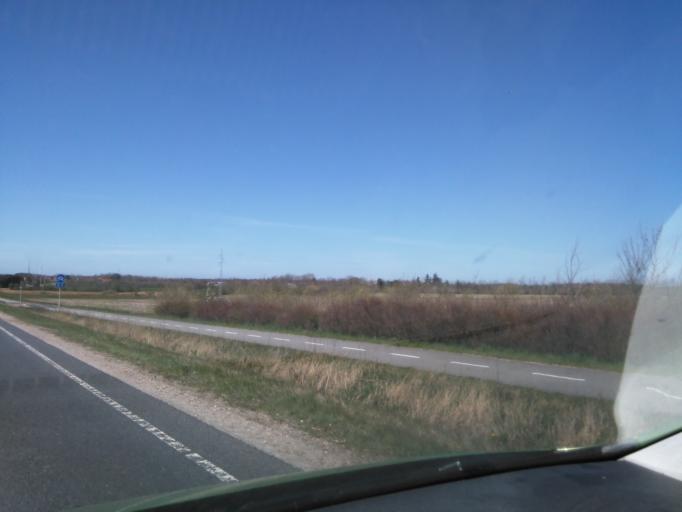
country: DK
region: South Denmark
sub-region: Varde Kommune
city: Oksbol
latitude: 55.6182
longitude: 8.3146
